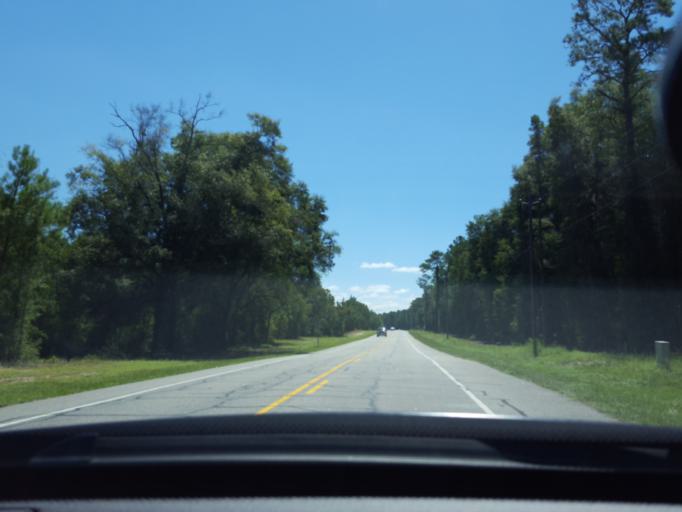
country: US
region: North Carolina
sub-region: Bladen County
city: Elizabethtown
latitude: 34.6464
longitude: -78.5178
